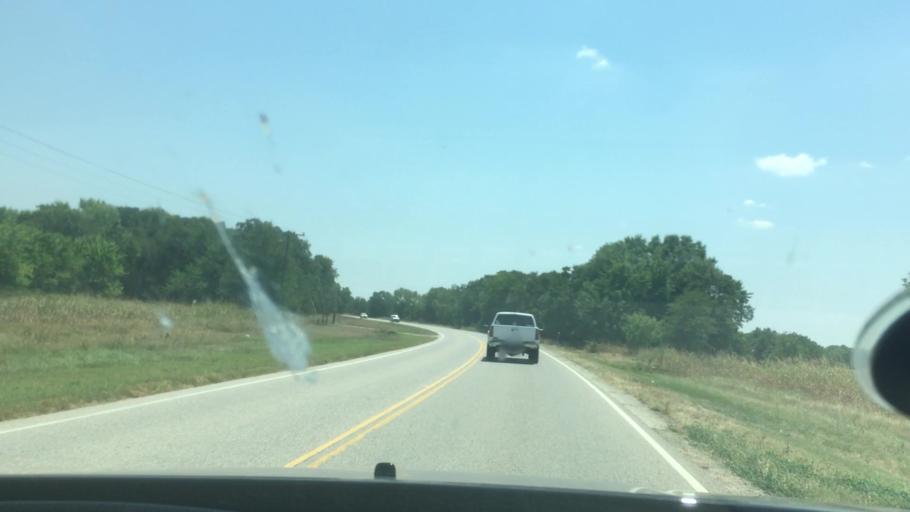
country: US
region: Oklahoma
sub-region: Bryan County
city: Durant
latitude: 34.1785
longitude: -96.4162
